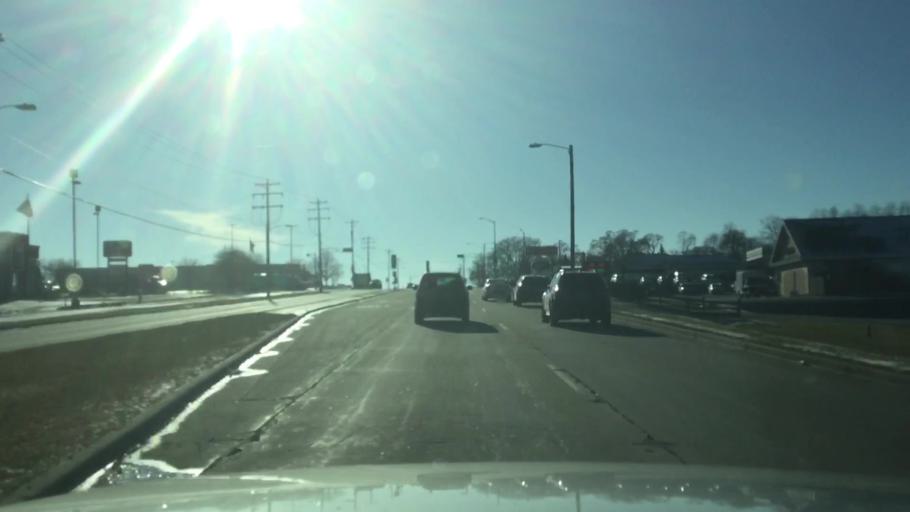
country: US
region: Wisconsin
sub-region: Racine County
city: Burlington
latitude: 42.6933
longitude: -88.2644
